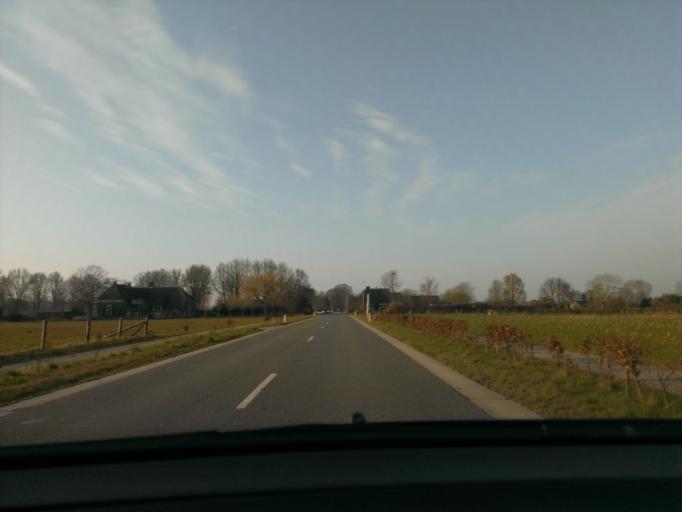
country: NL
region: Gelderland
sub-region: Gemeente Voorst
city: Twello
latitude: 52.2543
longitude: 6.1117
